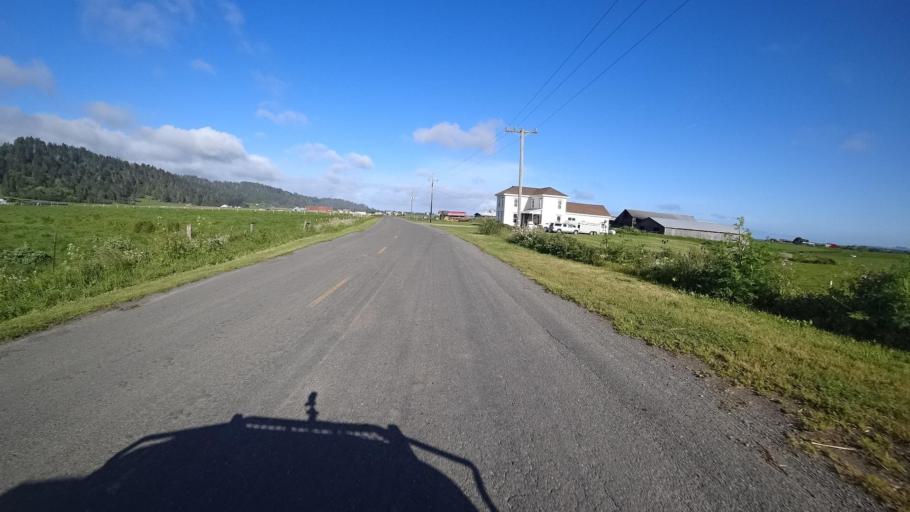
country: US
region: California
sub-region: Humboldt County
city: Ferndale
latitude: 40.5707
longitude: -124.2232
